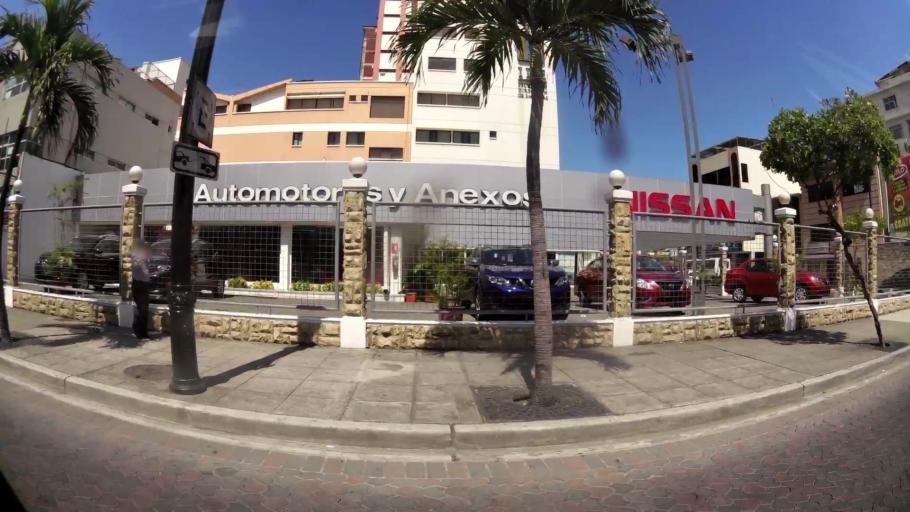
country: EC
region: Guayas
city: Guayaquil
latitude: -2.1872
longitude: -79.8959
